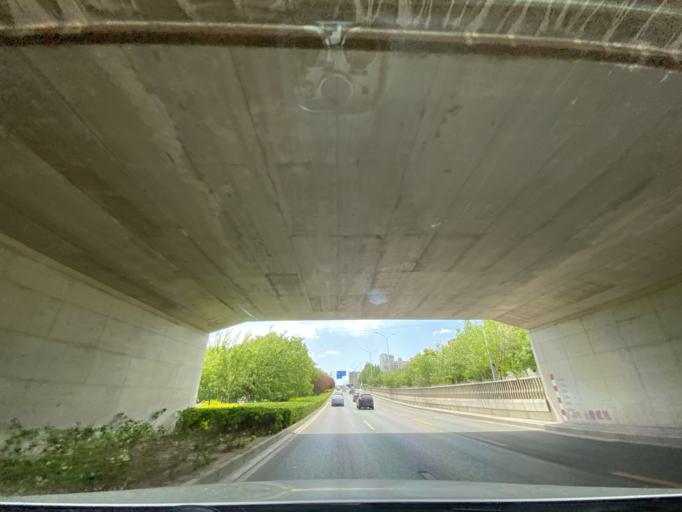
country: CN
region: Beijing
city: Sijiqing
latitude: 39.9315
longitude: 116.2468
